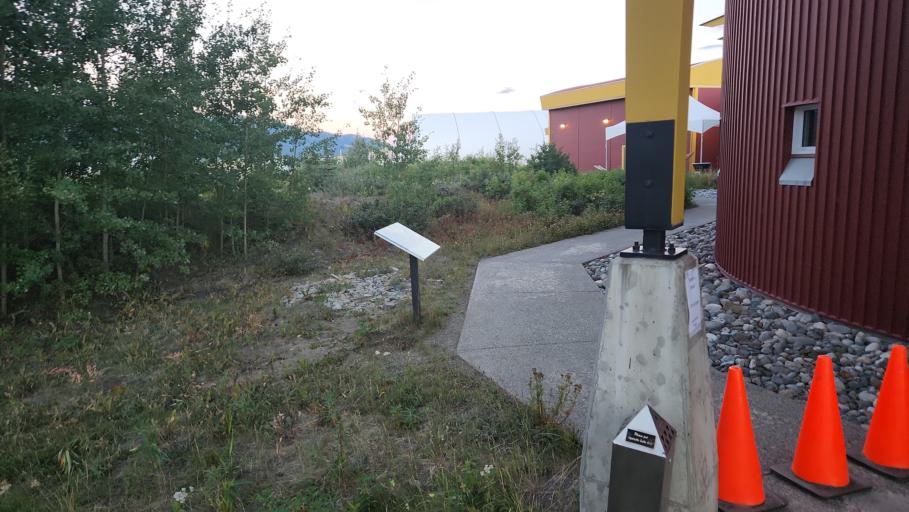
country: CA
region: Yukon
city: Whitehorse
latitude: 60.7091
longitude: -135.0792
